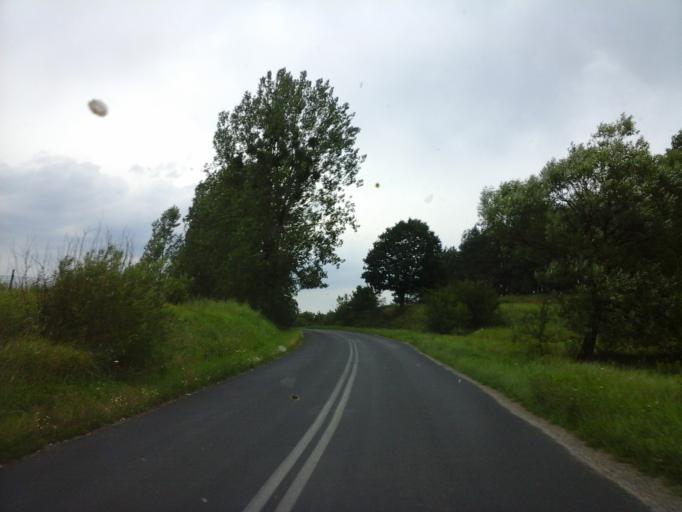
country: PL
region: West Pomeranian Voivodeship
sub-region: Powiat choszczenski
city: Choszczno
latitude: 53.1346
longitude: 15.4563
